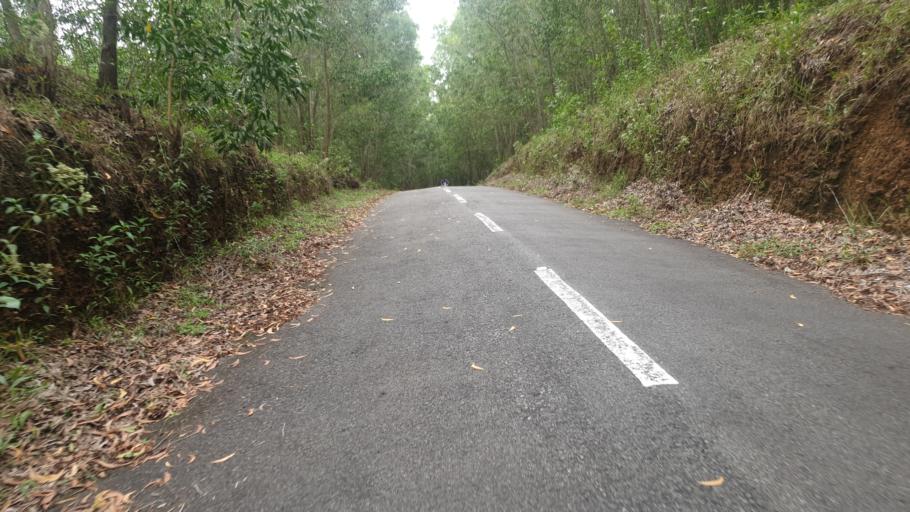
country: IN
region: Kerala
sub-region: Thiruvananthapuram
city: Nedumangad
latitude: 8.6329
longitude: 77.1163
